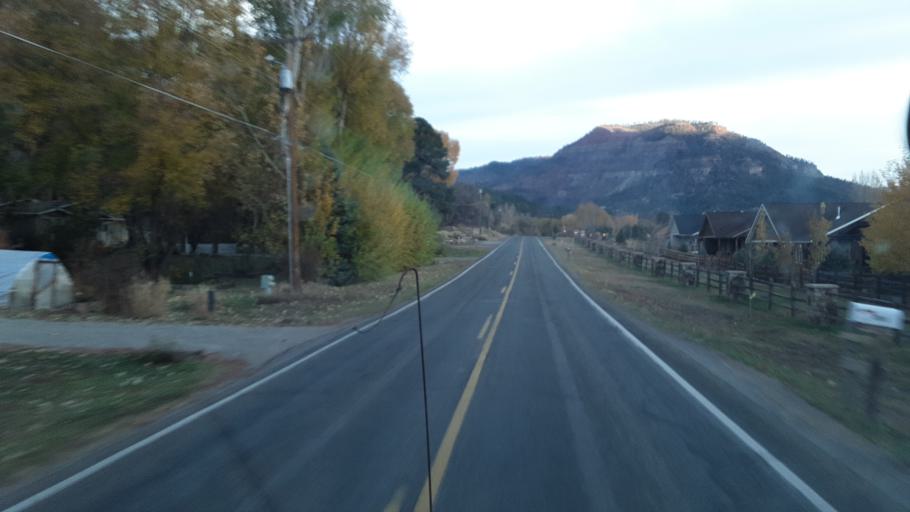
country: US
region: Colorado
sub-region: La Plata County
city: Durango
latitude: 37.3989
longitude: -107.8467
